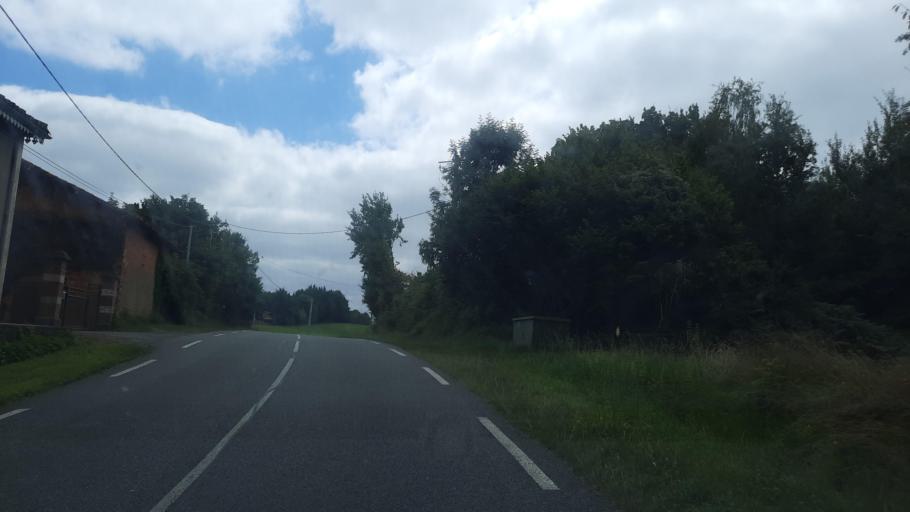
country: FR
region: Midi-Pyrenees
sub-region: Departement des Hautes-Pyrenees
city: Trie-sur-Baise
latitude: 43.3077
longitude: 0.3798
